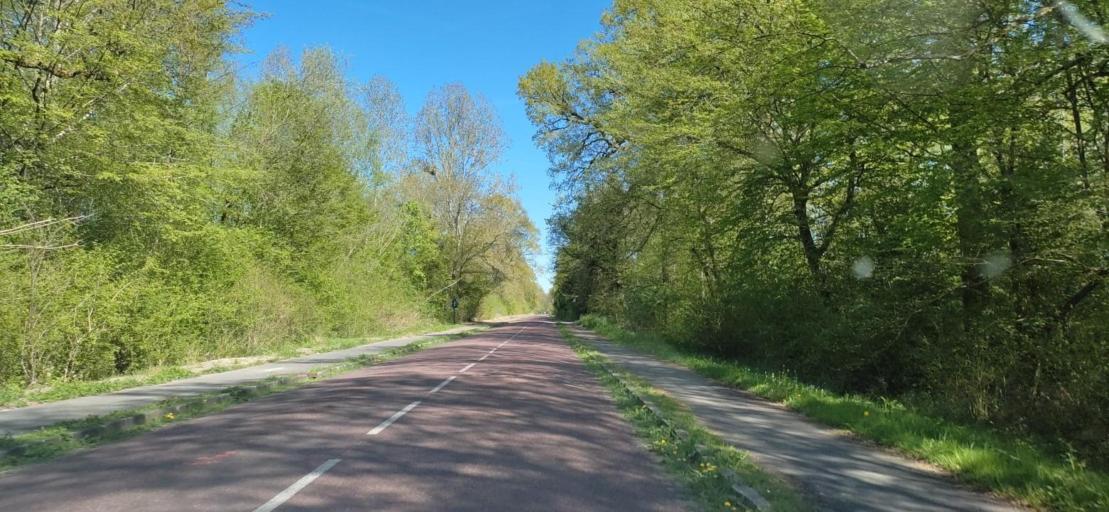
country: FR
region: Picardie
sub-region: Departement de l'Oise
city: Choisy-au-Bac
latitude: 49.4275
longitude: 2.8917
